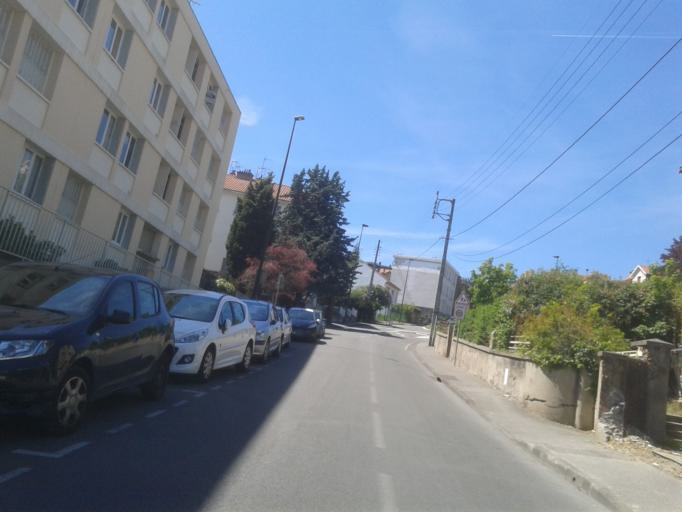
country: FR
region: Auvergne
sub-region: Departement du Puy-de-Dome
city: Chamalieres
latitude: 45.7676
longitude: 3.0674
